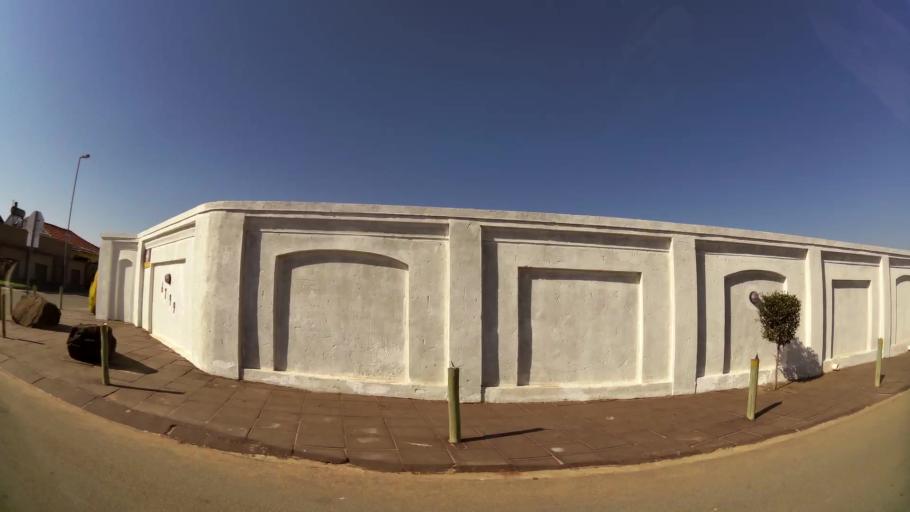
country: ZA
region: Gauteng
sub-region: Ekurhuleni Metropolitan Municipality
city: Tembisa
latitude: -26.0397
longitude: 28.2006
